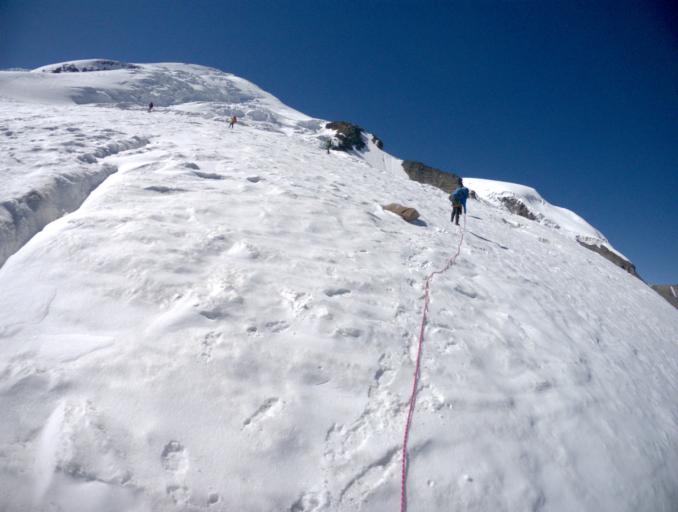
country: RU
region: Kabardino-Balkariya
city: Terskol
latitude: 43.3836
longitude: 42.4367
